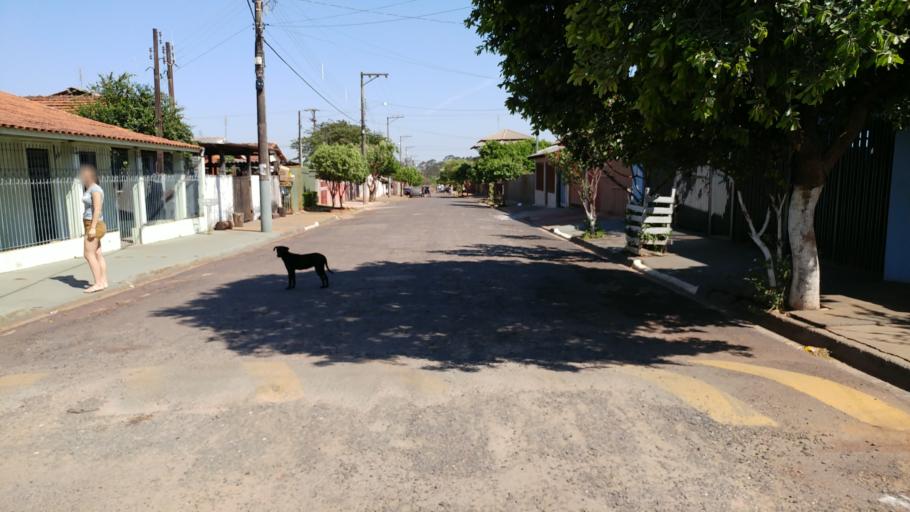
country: BR
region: Sao Paulo
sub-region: Paraguacu Paulista
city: Paraguacu Paulista
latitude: -22.4236
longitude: -50.5885
